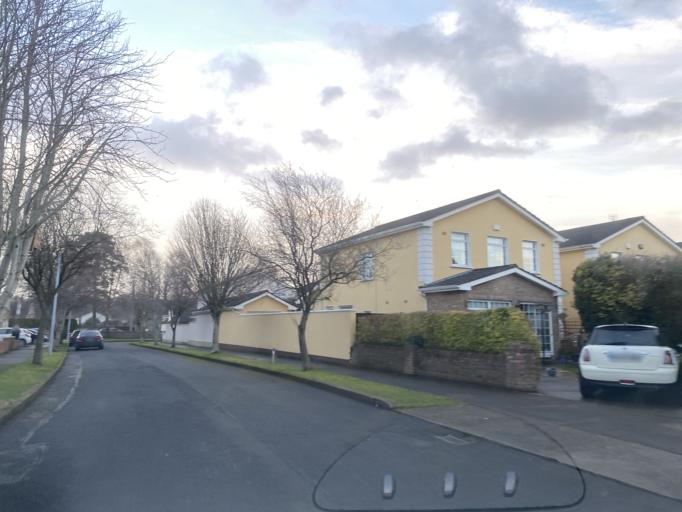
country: IE
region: Leinster
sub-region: Kildare
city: Celbridge
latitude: 53.3482
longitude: -6.5438
